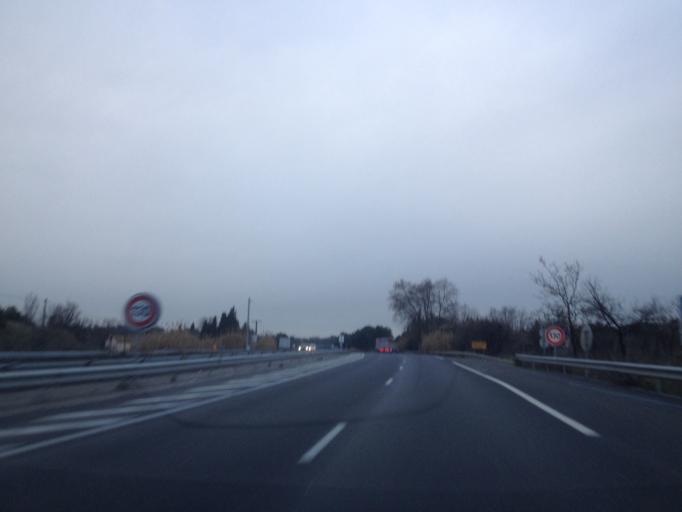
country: FR
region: Provence-Alpes-Cote d'Azur
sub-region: Departement des Bouches-du-Rhone
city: Aix-en-Provence
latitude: 43.5195
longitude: 5.4264
